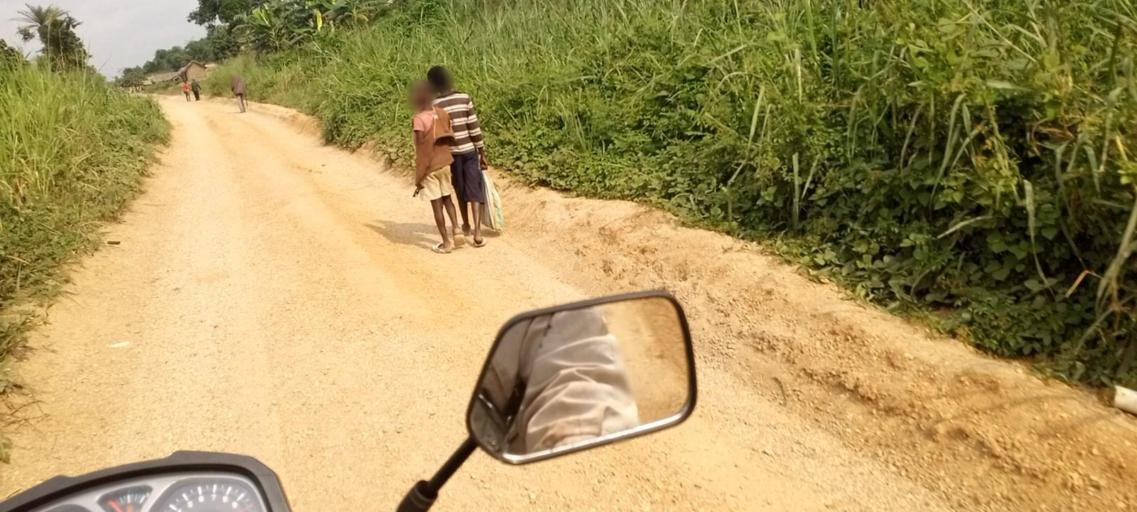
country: CD
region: Eastern Province
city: Kisangani
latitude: 0.2948
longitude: 25.4659
